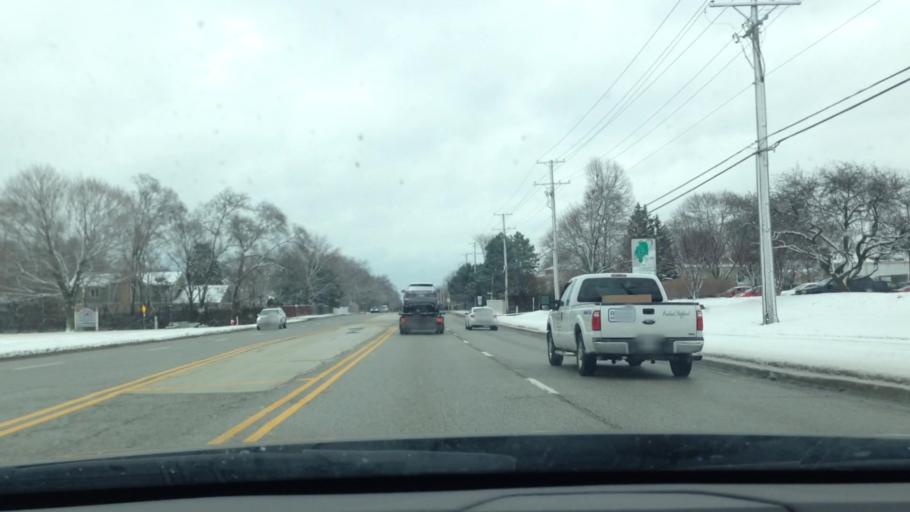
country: US
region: Illinois
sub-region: Cook County
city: Northbrook
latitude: 42.1057
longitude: -87.8469
